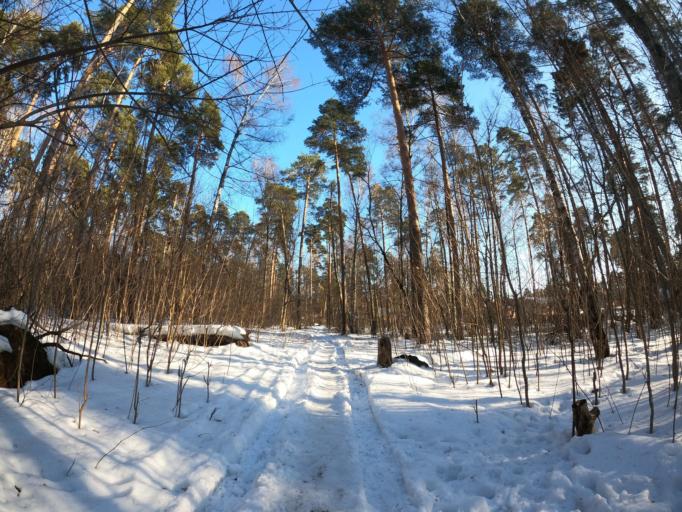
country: RU
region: Moskovskaya
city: Kraskovo
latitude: 55.6395
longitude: 37.9950
